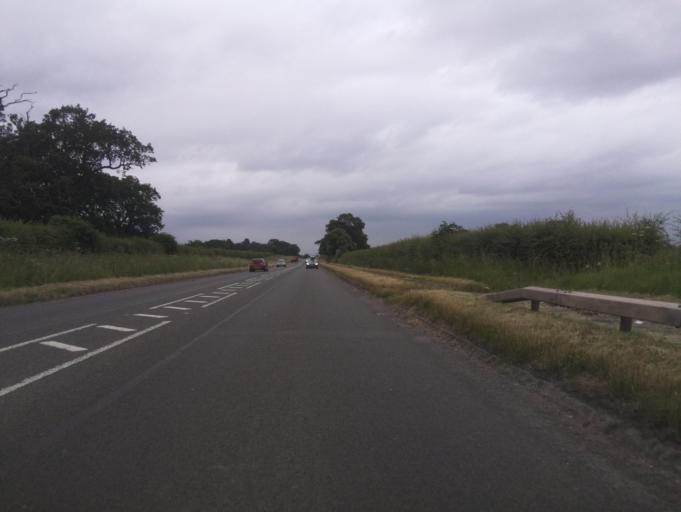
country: GB
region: England
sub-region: Staffordshire
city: Penkridge
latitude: 52.7500
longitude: -2.1071
